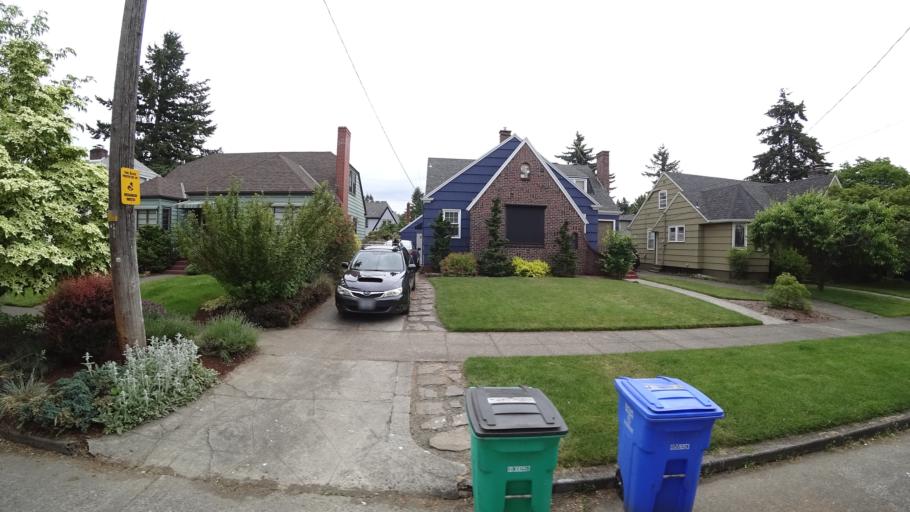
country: US
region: Oregon
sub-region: Multnomah County
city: Lents
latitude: 45.5357
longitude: -122.6037
